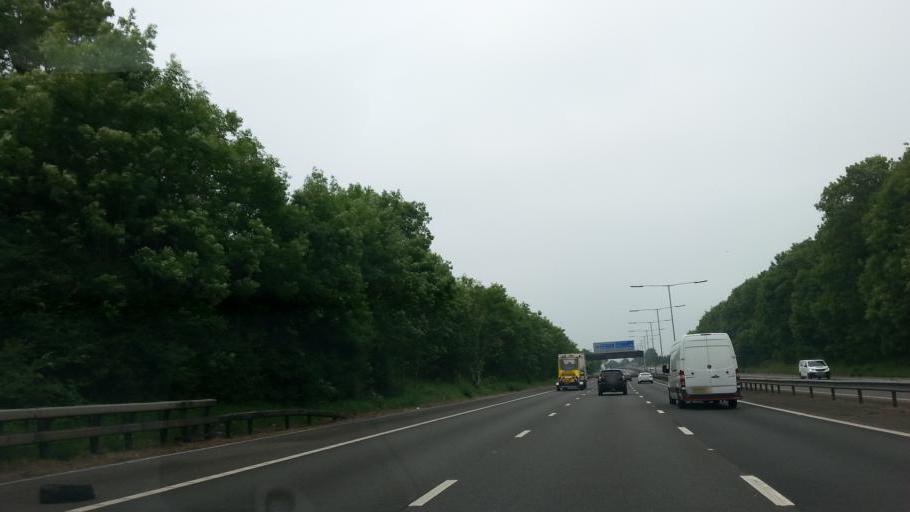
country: GB
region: England
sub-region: Warwickshire
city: Bedworth
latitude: 52.4555
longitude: -1.4179
